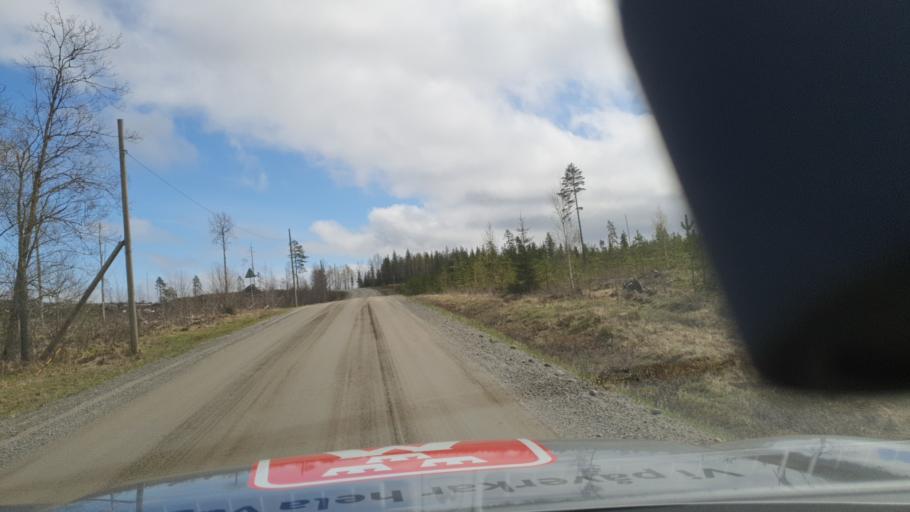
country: SE
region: Vaesterbotten
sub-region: Bjurholms Kommun
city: Bjurholm
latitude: 63.7049
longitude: 18.9107
